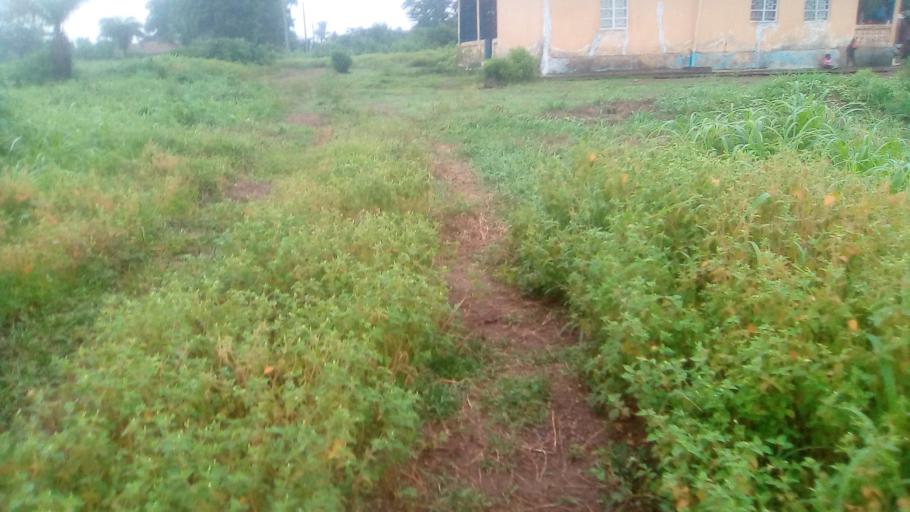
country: SL
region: Southern Province
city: Moyamba
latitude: 8.1499
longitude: -12.4308
